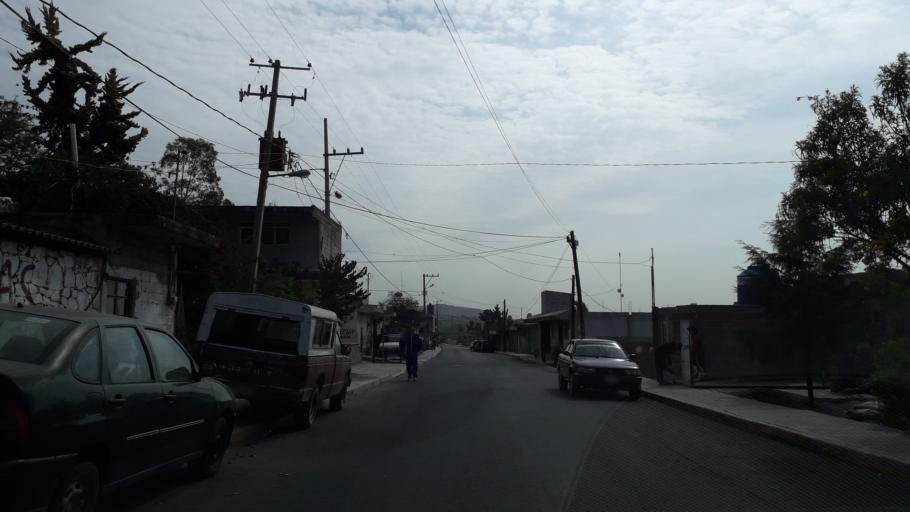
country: MX
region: Puebla
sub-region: Puebla
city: San Andres Azumiatla
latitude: 18.9063
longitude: -98.2468
